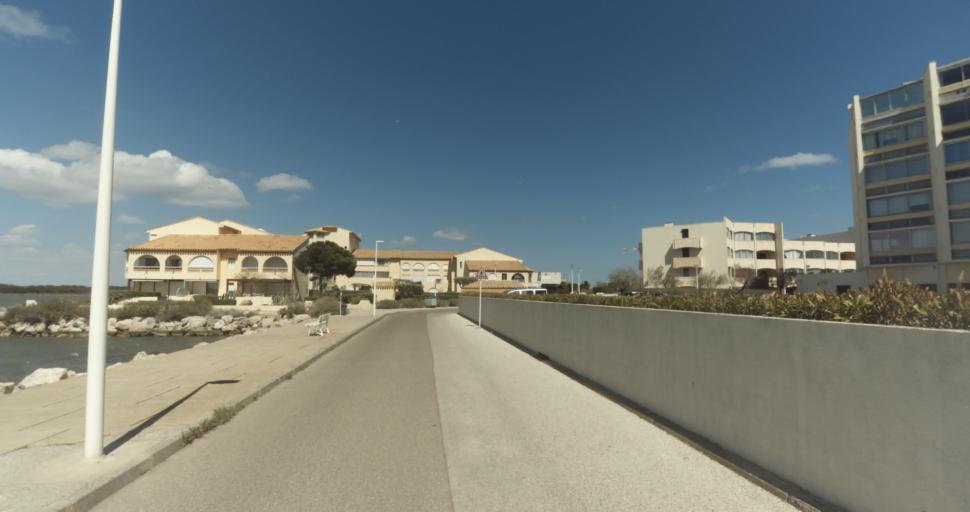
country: FR
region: Languedoc-Roussillon
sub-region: Departement de l'Aude
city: Leucate
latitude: 42.8614
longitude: 3.0361
